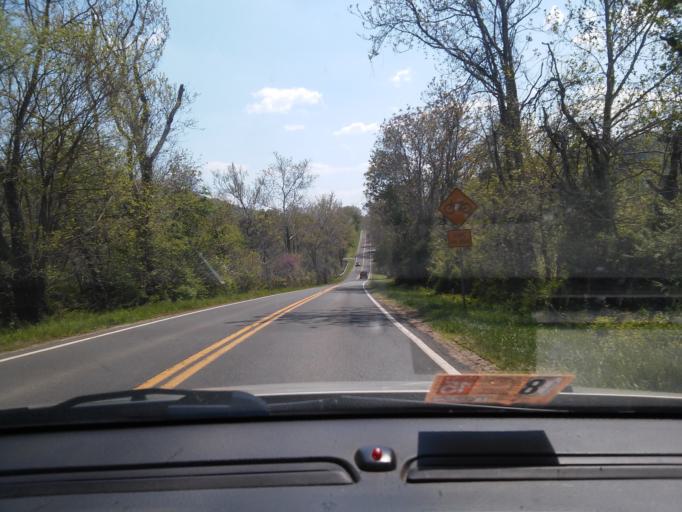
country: US
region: Virginia
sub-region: Rappahannock County
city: Washington
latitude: 38.7576
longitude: -78.1002
